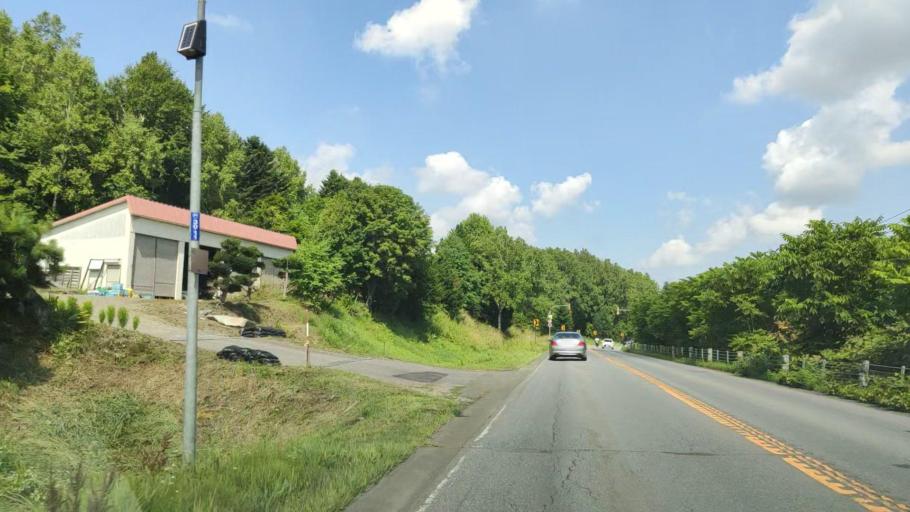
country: JP
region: Hokkaido
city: Shimo-furano
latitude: 43.5555
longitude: 142.4356
